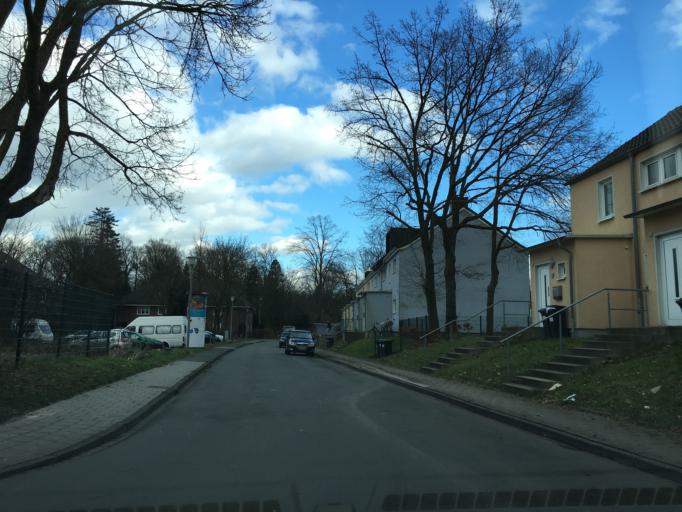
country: DE
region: North Rhine-Westphalia
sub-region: Regierungsbezirk Munster
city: Muenster
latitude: 51.9430
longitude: 7.6541
